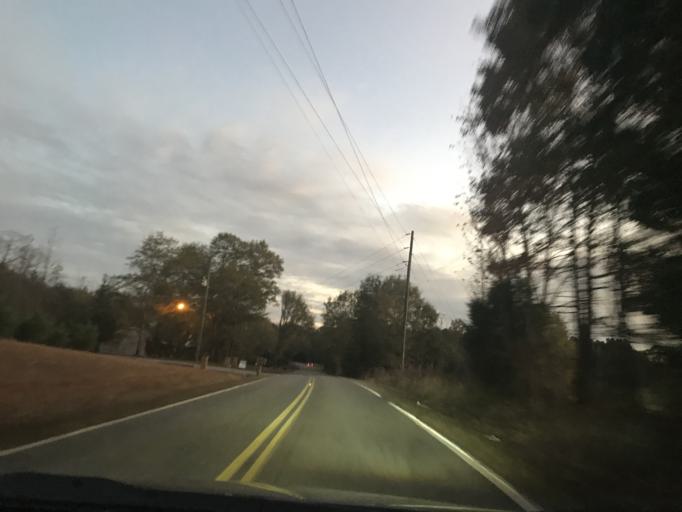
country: US
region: South Carolina
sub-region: Spartanburg County
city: Mayo
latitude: 35.0688
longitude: -81.9000
